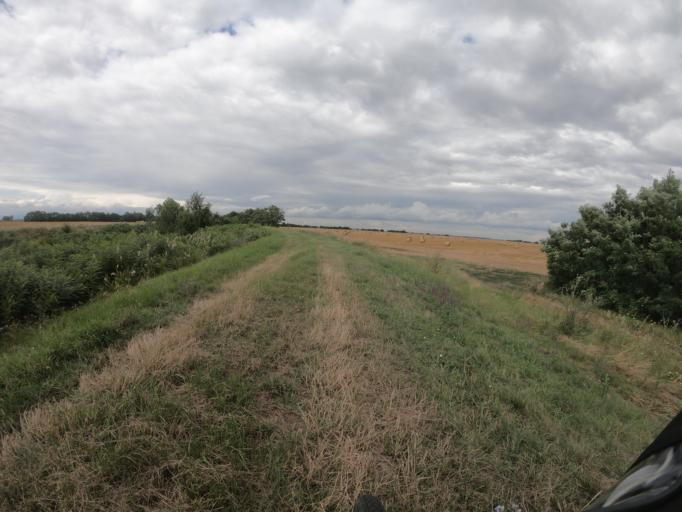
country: HU
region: Borsod-Abauj-Zemplen
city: Szentistvan
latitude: 47.7260
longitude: 20.7051
